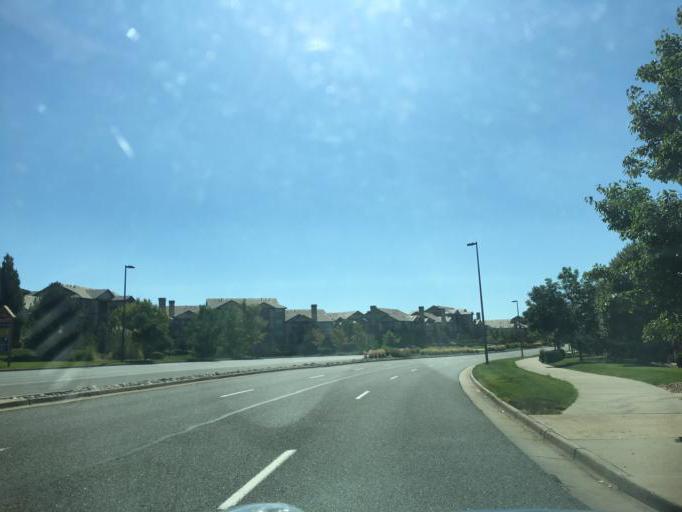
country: US
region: Colorado
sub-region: Douglas County
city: Parker
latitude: 39.5943
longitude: -104.7241
